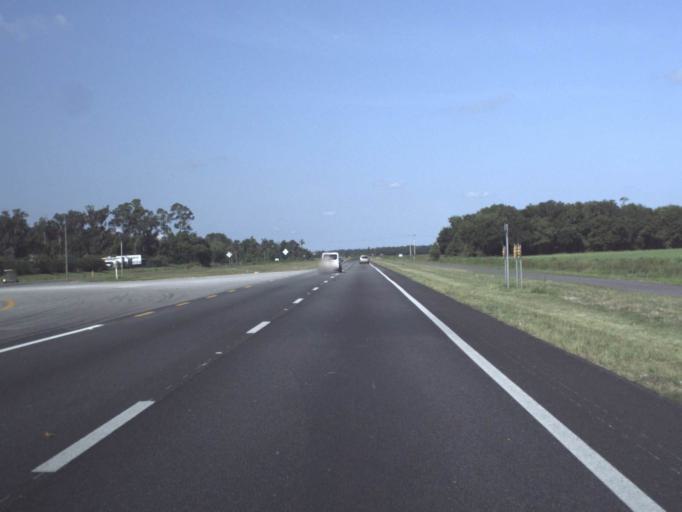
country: US
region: Florida
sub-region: Putnam County
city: East Palatka
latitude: 29.7090
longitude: -81.5326
